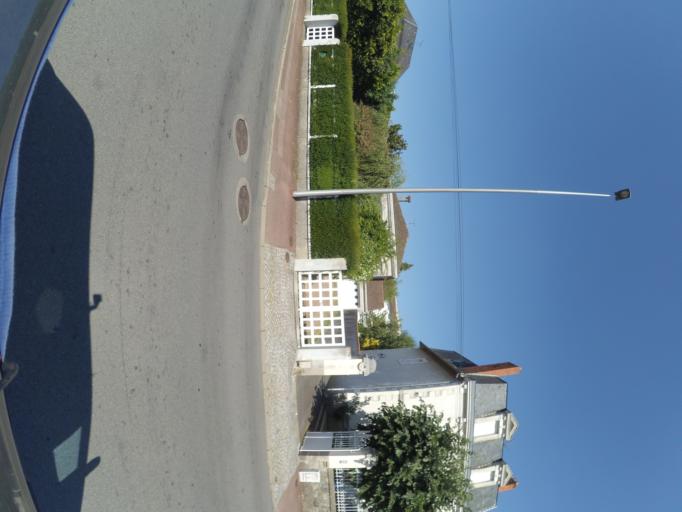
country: FR
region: Limousin
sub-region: Departement de la Haute-Vienne
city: Limoges
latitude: 45.8250
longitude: 1.2793
